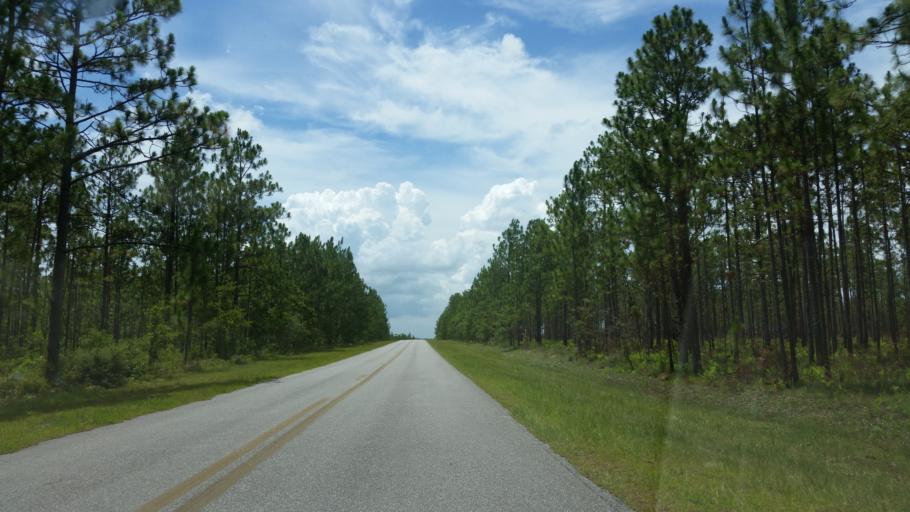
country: US
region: Florida
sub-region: Okaloosa County
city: Crestview
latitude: 30.7152
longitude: -86.7778
